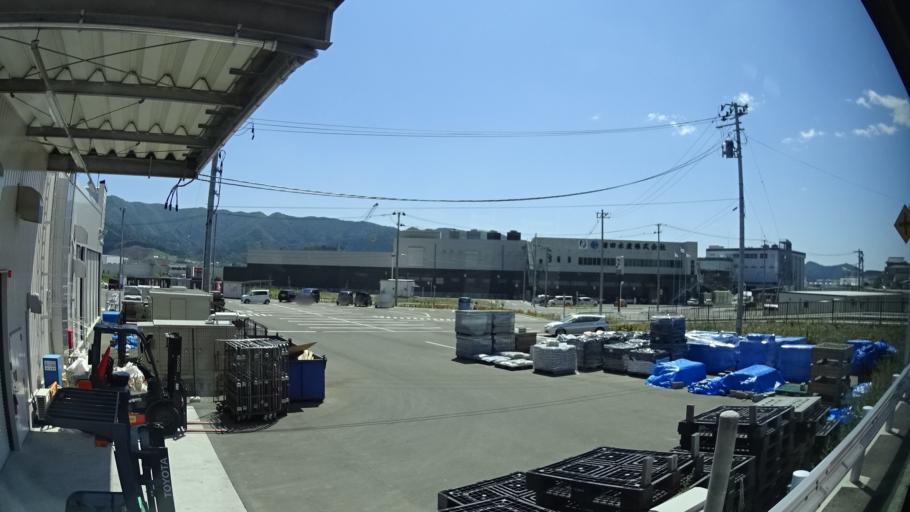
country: JP
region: Iwate
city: Ofunato
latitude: 39.0579
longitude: 141.7209
